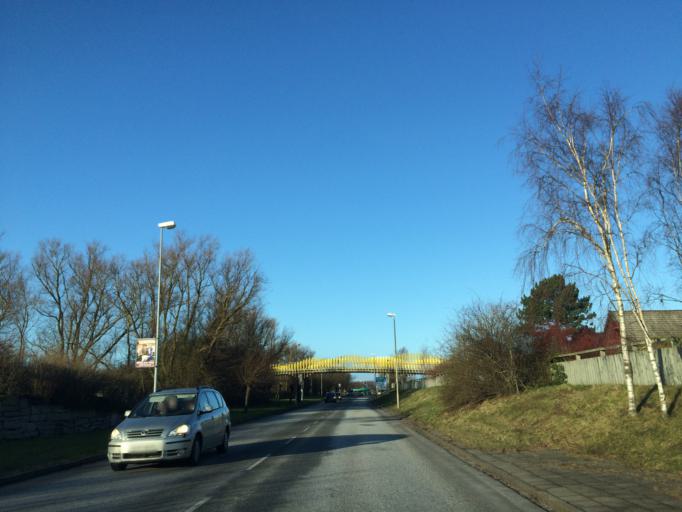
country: SE
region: Skane
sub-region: Malmo
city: Bunkeflostrand
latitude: 55.5667
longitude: 12.9598
